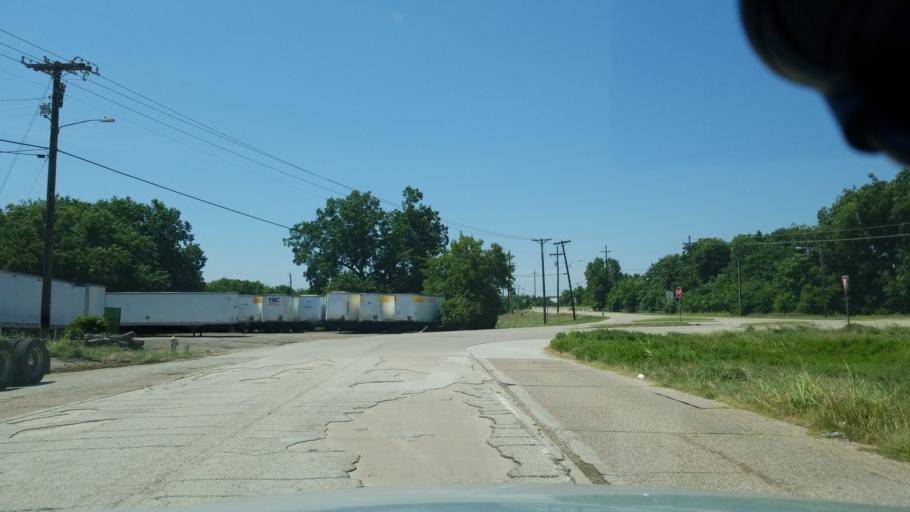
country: US
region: Texas
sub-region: Tarrant County
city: Euless
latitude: 32.8348
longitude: -97.0300
